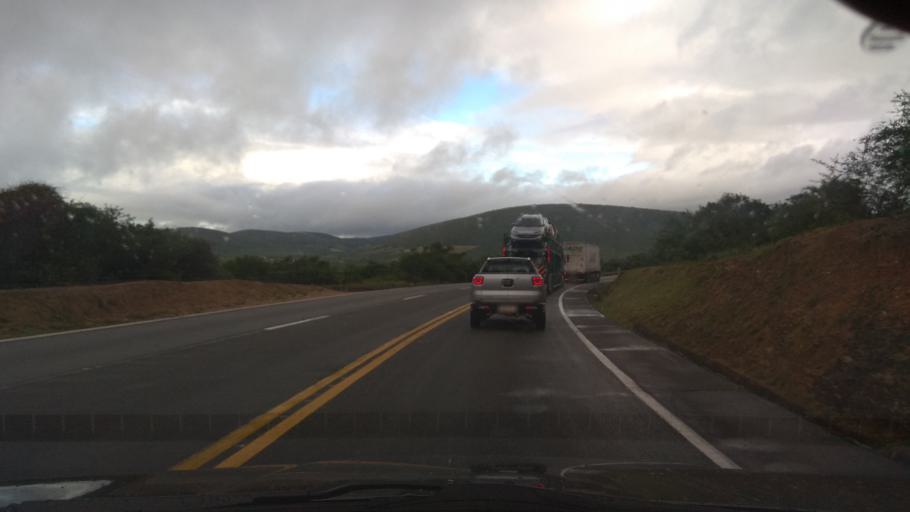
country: BR
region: Bahia
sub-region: Santa Ines
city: Santa Ines
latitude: -13.2541
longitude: -40.0121
